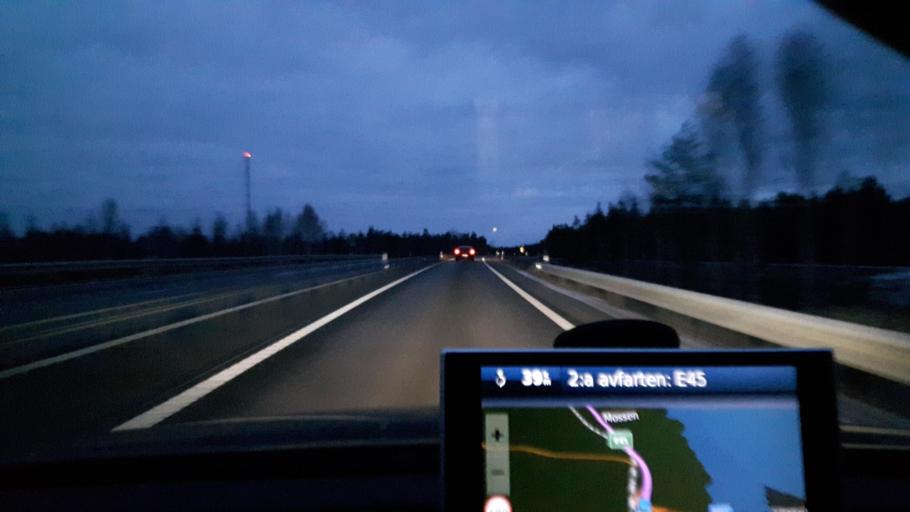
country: SE
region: Vaestra Goetaland
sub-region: Vanersborgs Kommun
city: Vanersborg
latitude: 58.3887
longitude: 12.2904
